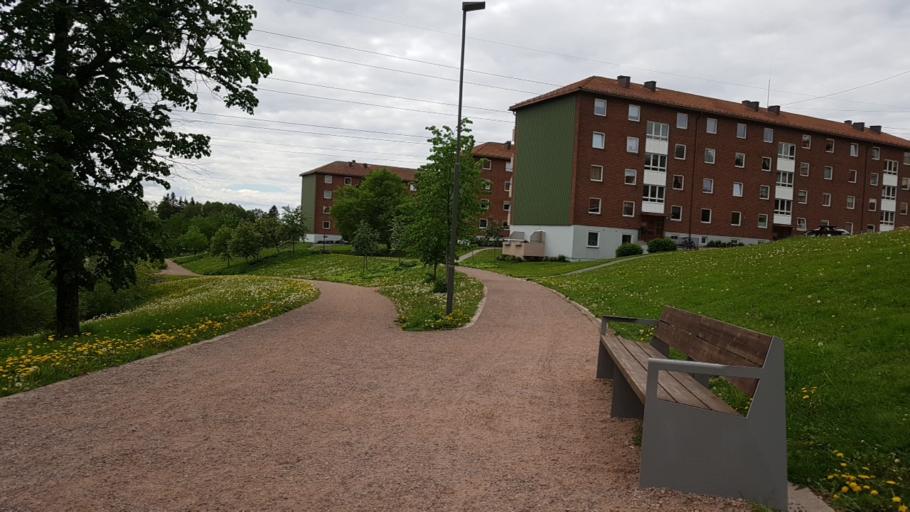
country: NO
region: Oslo
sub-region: Oslo
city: Oslo
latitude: 59.9398
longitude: 10.8214
